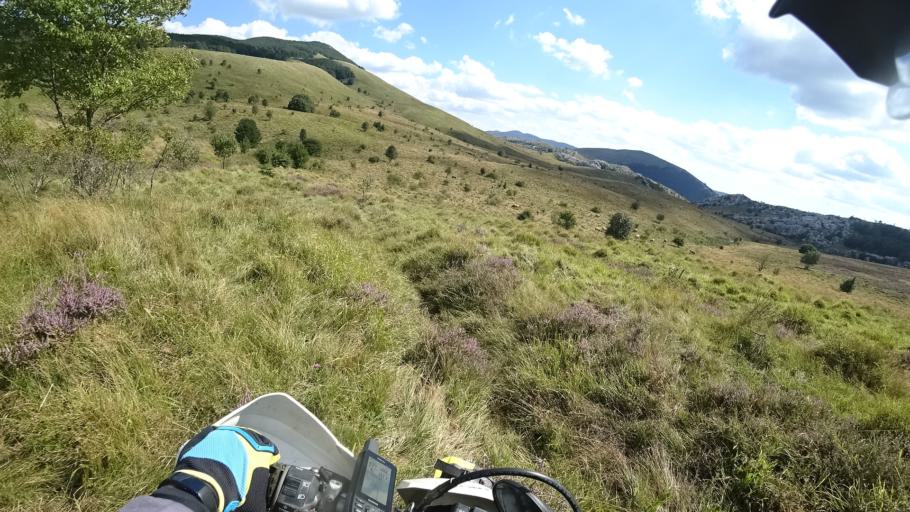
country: HR
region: Zadarska
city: Gracac
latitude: 44.4171
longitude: 16.0008
